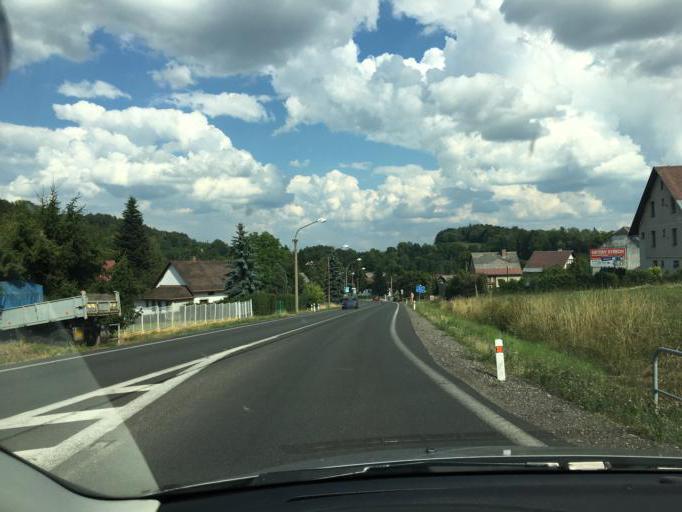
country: CZ
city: Horni Branna
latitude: 50.6214
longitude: 15.5546
